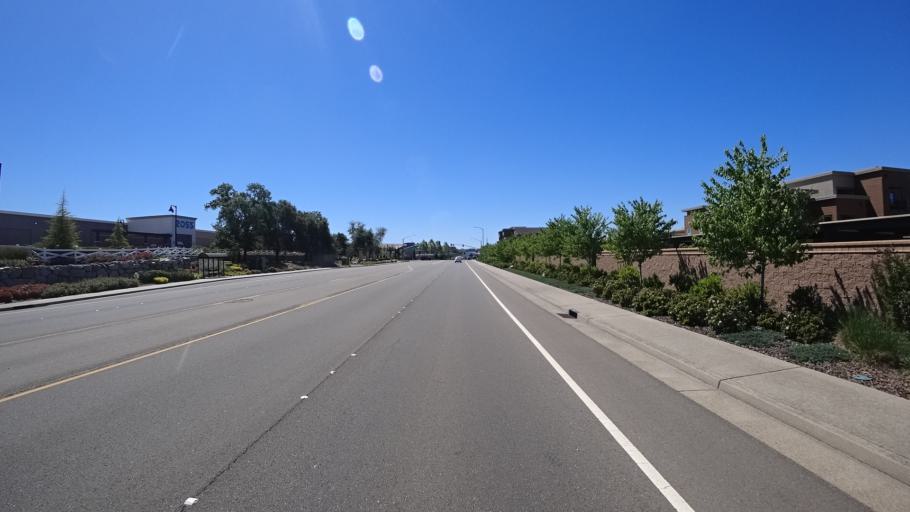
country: US
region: California
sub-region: Placer County
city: Loomis
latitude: 38.8038
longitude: -121.2103
